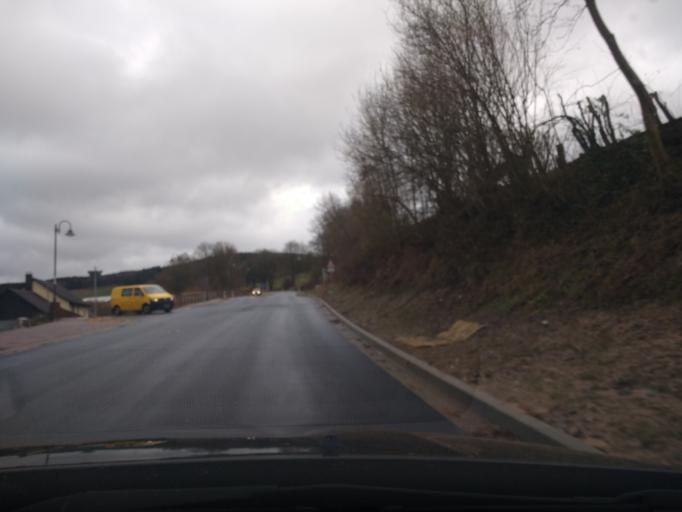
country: DE
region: Rheinland-Pfalz
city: Zerf
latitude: 49.6008
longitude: 6.6926
